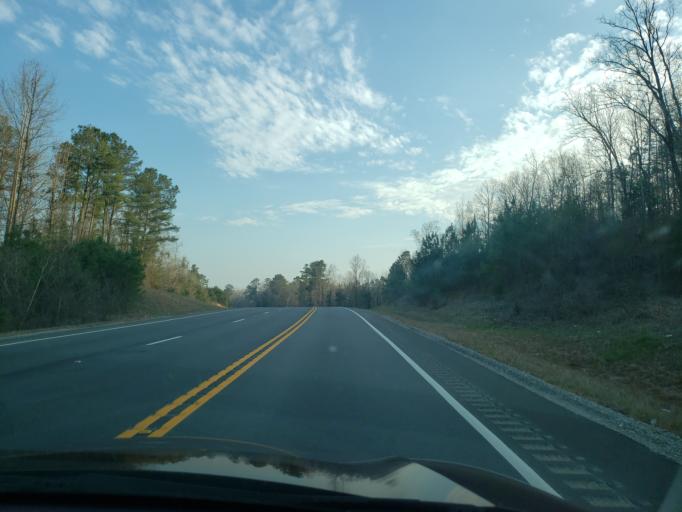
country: US
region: Alabama
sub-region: Hale County
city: Moundville
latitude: 32.8594
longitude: -87.6135
